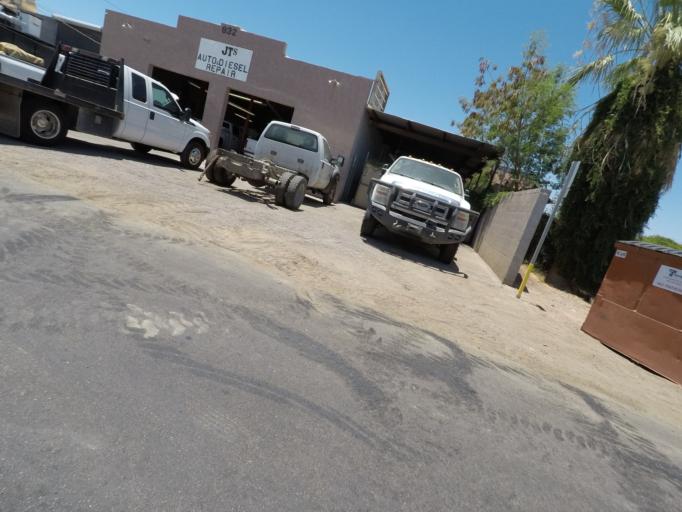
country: US
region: Arizona
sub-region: Maricopa County
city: Tempe
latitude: 33.4389
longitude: -111.9237
